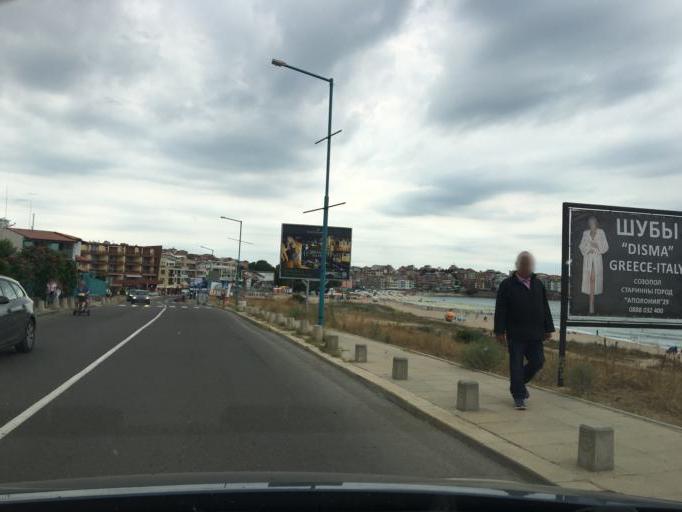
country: BG
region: Burgas
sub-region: Obshtina Sozopol
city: Sozopol
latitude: 42.4109
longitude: 27.7021
